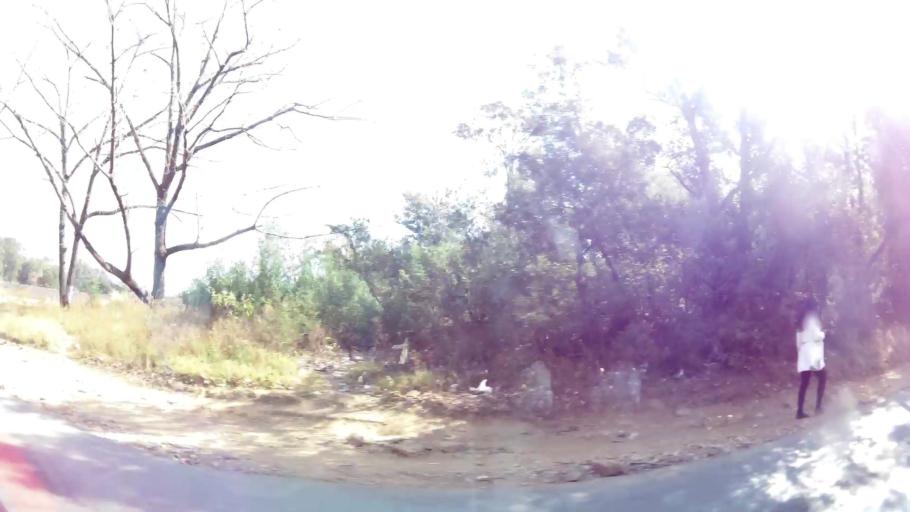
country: ZA
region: Gauteng
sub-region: City of Johannesburg Metropolitan Municipality
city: Roodepoort
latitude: -26.1767
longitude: 27.8717
